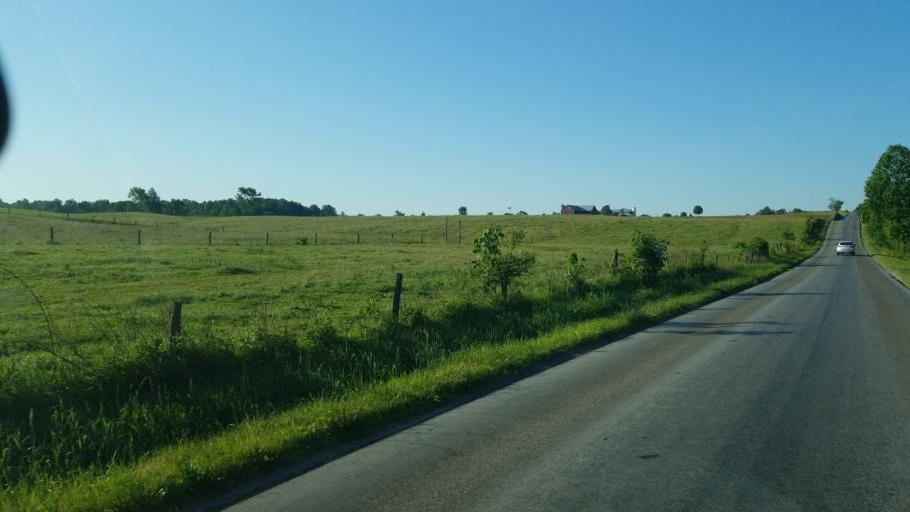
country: US
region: Ohio
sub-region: Wayne County
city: Apple Creek
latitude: 40.7040
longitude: -81.7844
